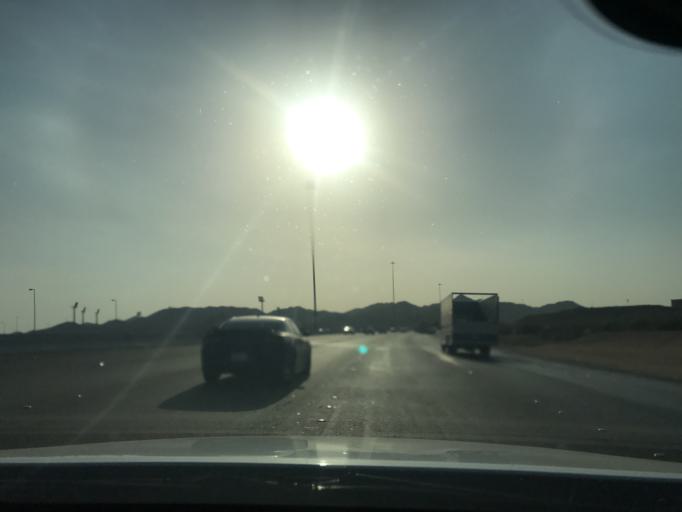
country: SA
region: Makkah
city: Jeddah
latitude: 21.3896
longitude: 39.4190
